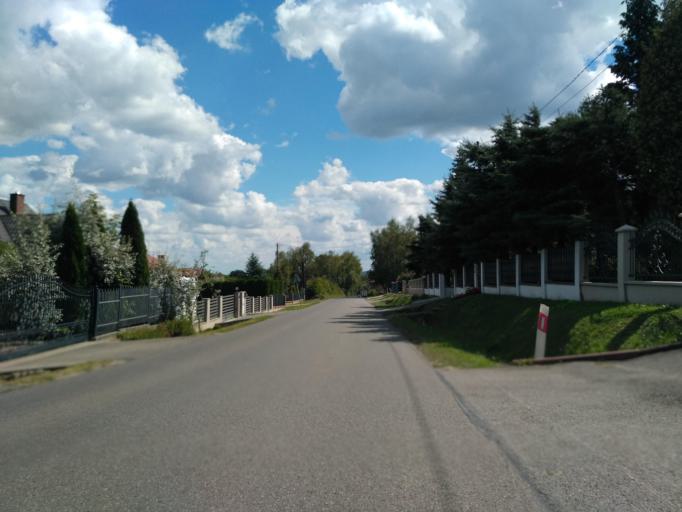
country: PL
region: Subcarpathian Voivodeship
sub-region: Powiat jasielski
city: Trzcinica
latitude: 49.7501
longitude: 21.4312
